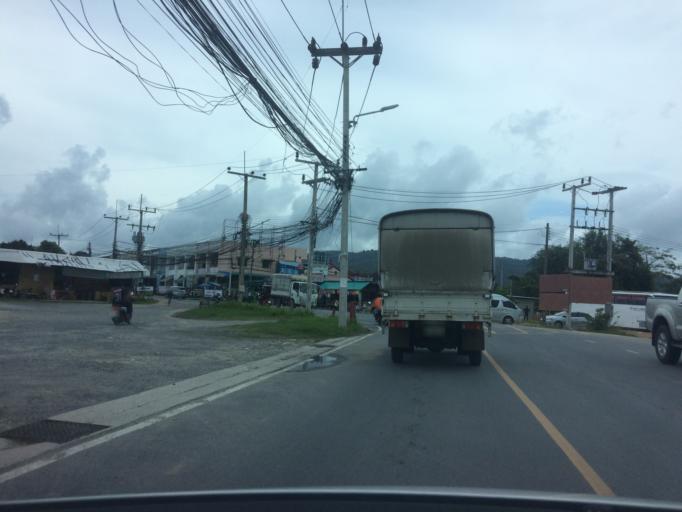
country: TH
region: Phuket
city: Mueang Phuket
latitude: 7.8622
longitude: 98.3670
